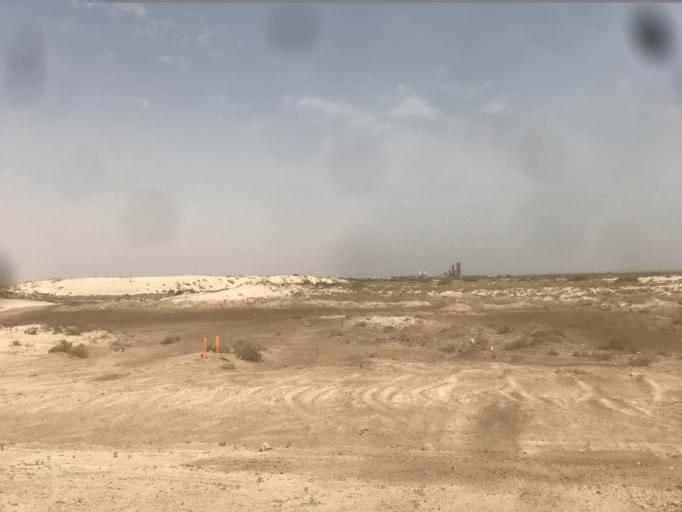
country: SA
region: Eastern Province
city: Abqaiq
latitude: 25.9056
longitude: 50.0137
